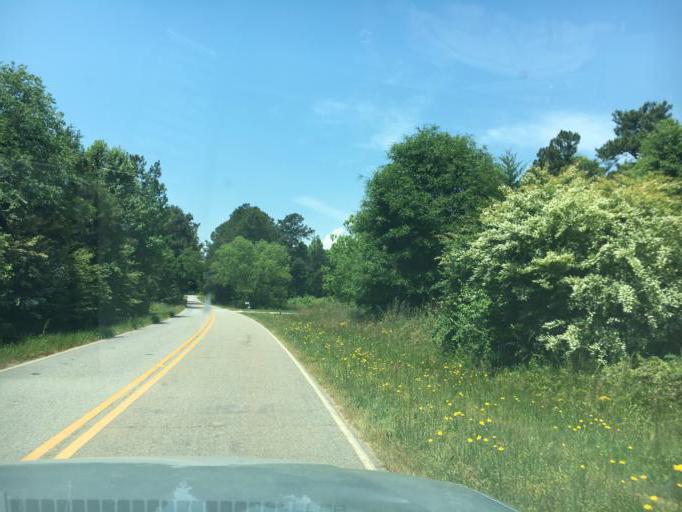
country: US
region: Georgia
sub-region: Hart County
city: Royston
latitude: 34.3050
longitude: -83.0959
